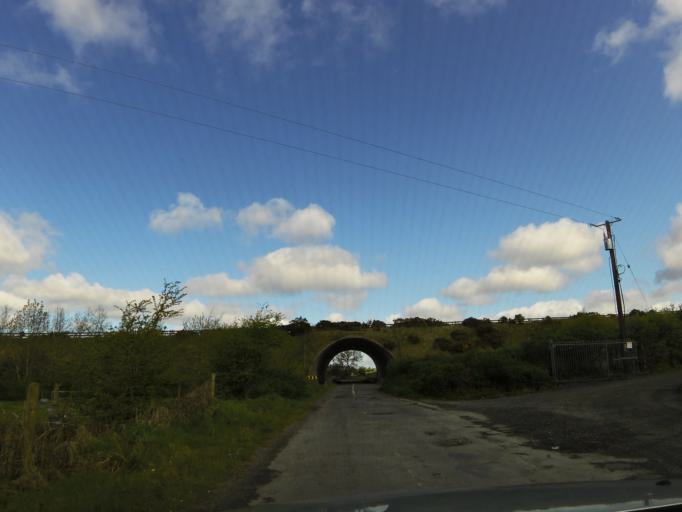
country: IE
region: Connaught
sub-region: Maigh Eo
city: Kiltamagh
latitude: 53.7862
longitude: -8.9376
